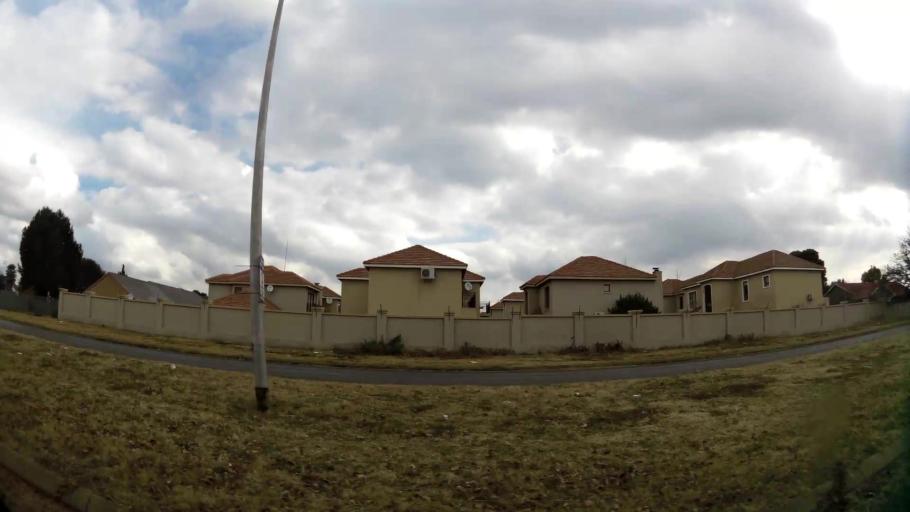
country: ZA
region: Gauteng
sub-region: Sedibeng District Municipality
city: Vanderbijlpark
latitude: -26.7299
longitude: 27.8535
